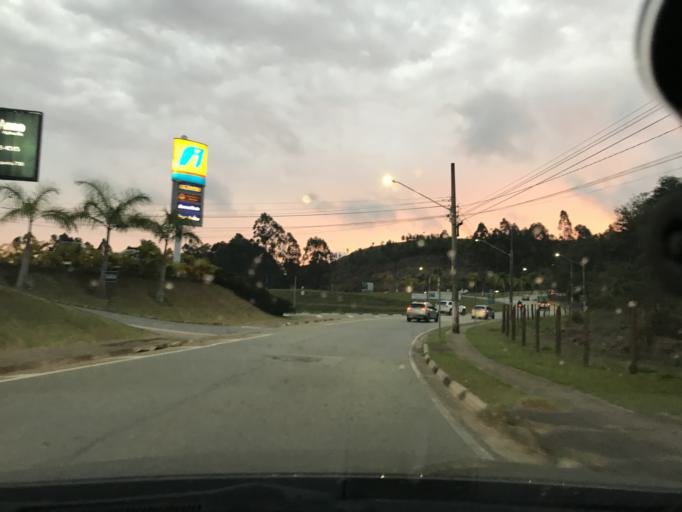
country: BR
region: Sao Paulo
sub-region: Barueri
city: Barueri
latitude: -23.4676
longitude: -46.8480
